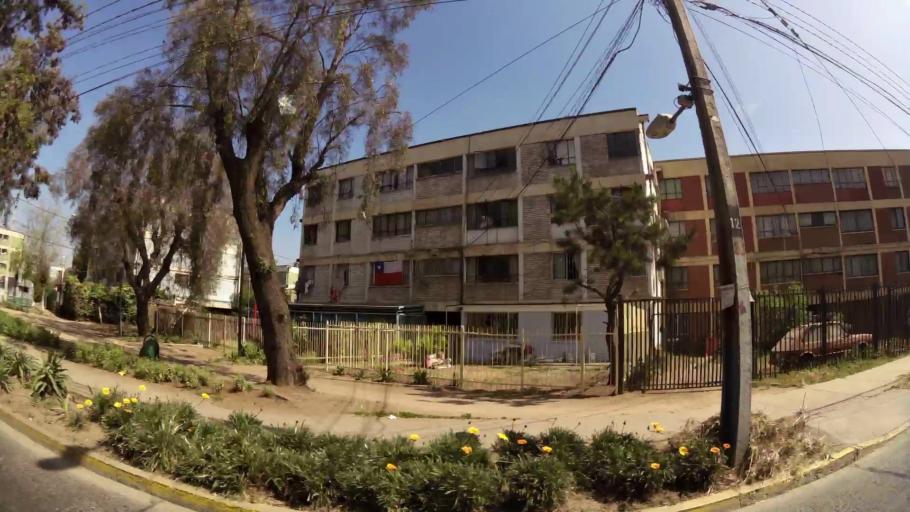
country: CL
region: Santiago Metropolitan
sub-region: Provincia de Santiago
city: Villa Presidente Frei, Nunoa, Santiago, Chile
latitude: -33.4655
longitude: -70.5504
